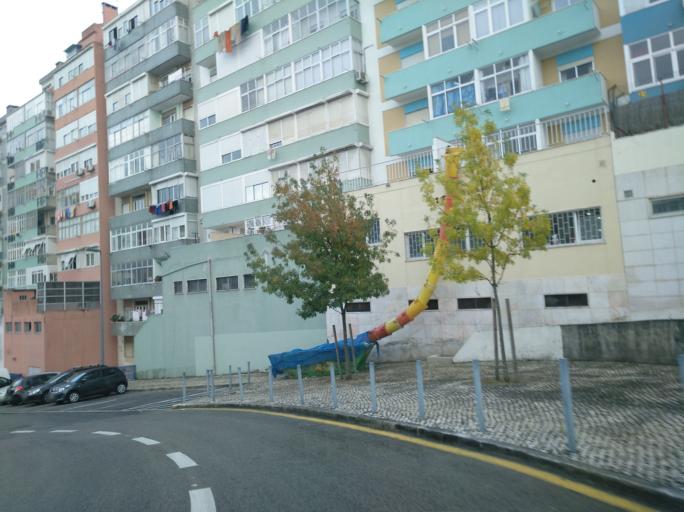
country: PT
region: Lisbon
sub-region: Odivelas
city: Pontinha
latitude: 38.7557
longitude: -9.1788
